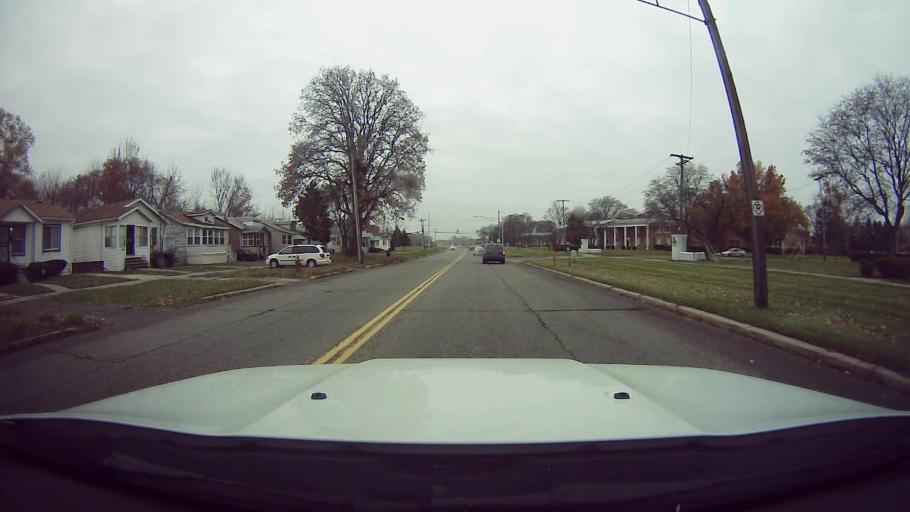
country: US
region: Michigan
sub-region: Wayne County
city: Dearborn Heights
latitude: 42.3335
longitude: -83.2350
